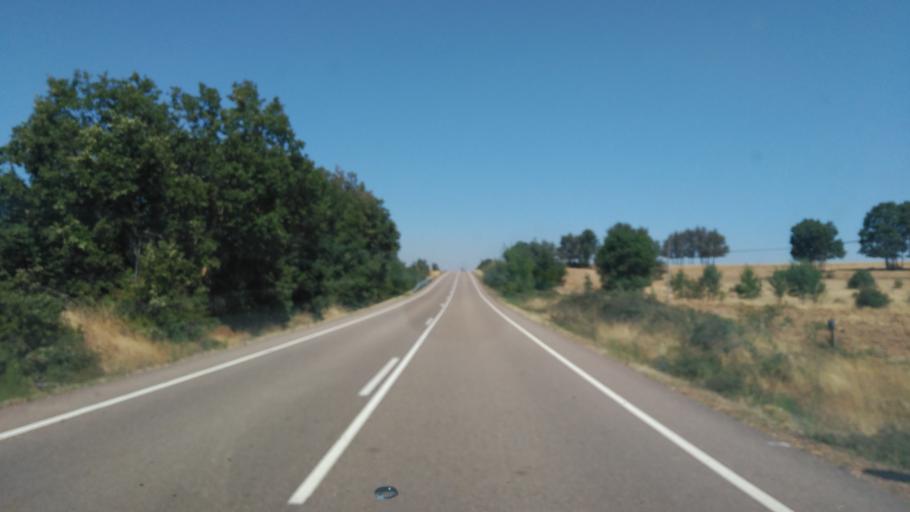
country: ES
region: Castille and Leon
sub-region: Provincia de Salamanca
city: Aldeanueva de la Sierra
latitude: 40.6316
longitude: -6.1088
